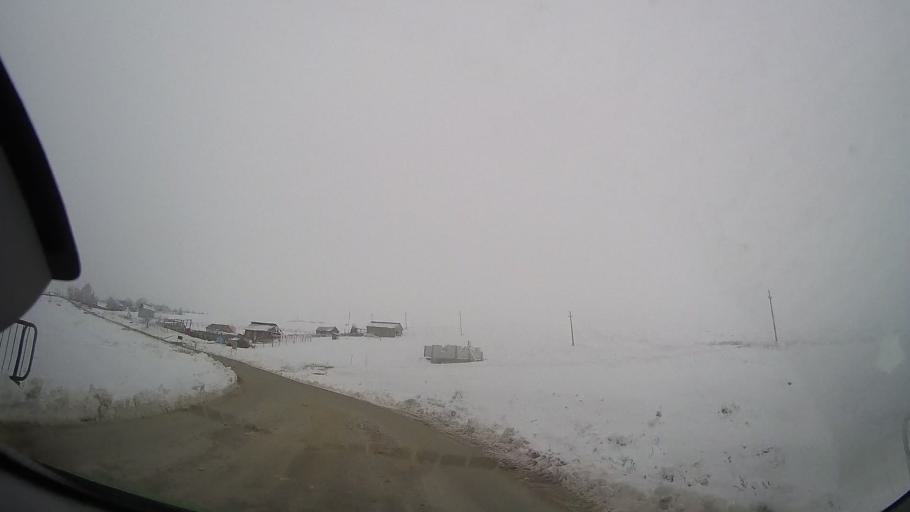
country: RO
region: Neamt
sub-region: Comuna Pancesti
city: Pancesti
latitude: 46.9132
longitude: 27.1610
